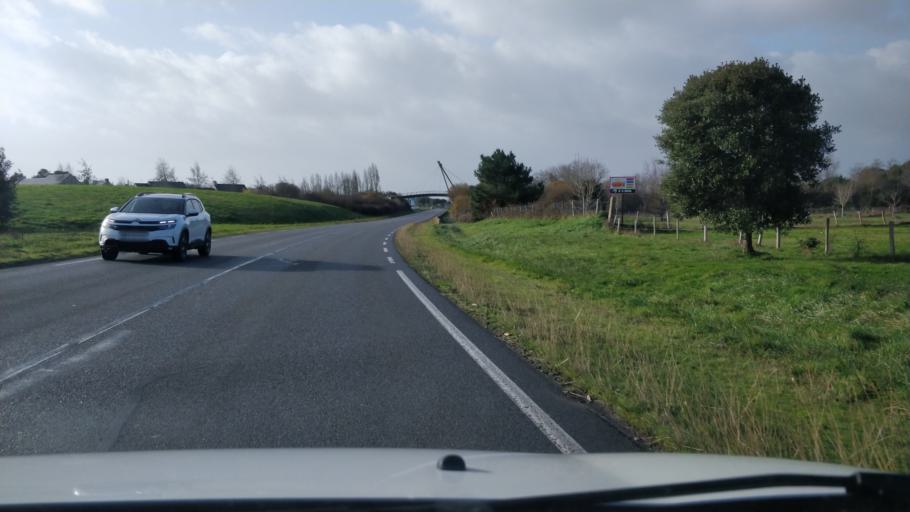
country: FR
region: Pays de la Loire
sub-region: Departement de la Loire-Atlantique
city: La Baule-Escoublac
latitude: 47.2975
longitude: -2.3929
